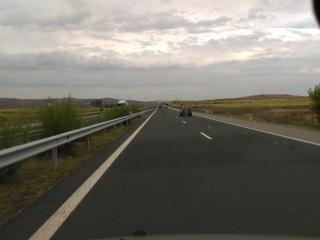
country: BG
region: Sliven
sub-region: Obshtina Sliven
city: Kermen
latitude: 42.4980
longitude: 26.2867
